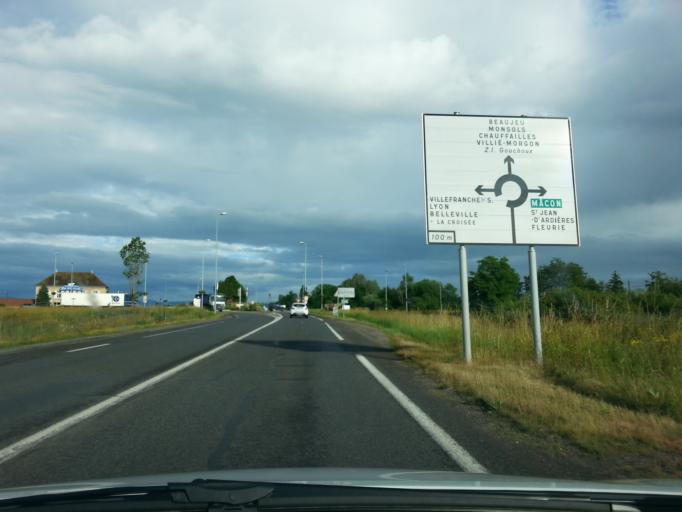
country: FR
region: Rhone-Alpes
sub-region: Departement du Rhone
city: Belleville
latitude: 46.1203
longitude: 4.7394
